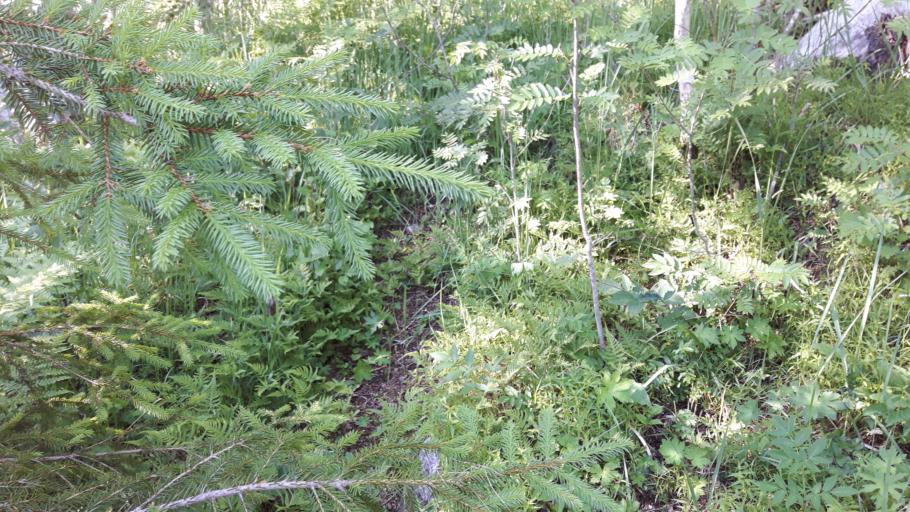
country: SE
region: Vaesternorrland
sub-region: Timra Kommun
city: Soraker
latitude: 62.6511
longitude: 17.5109
